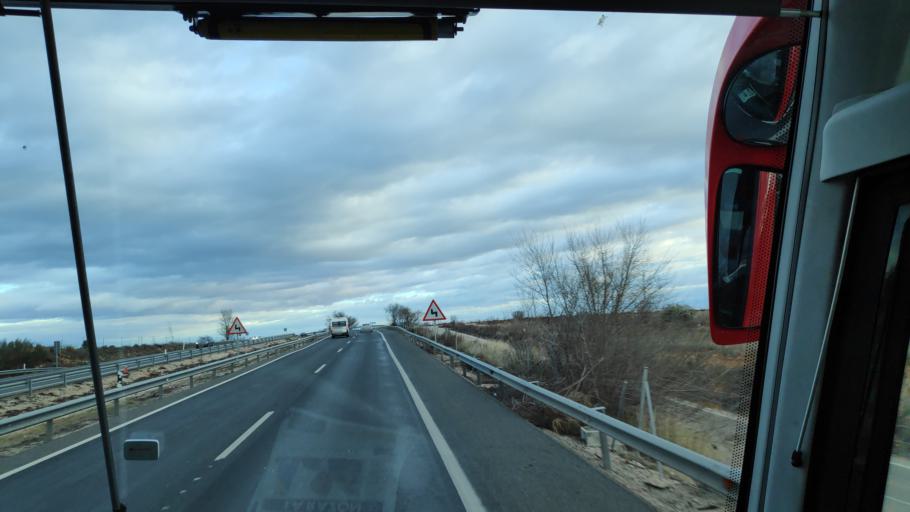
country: ES
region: Madrid
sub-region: Provincia de Madrid
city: Villarejo de Salvanes
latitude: 40.1587
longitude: -3.2610
